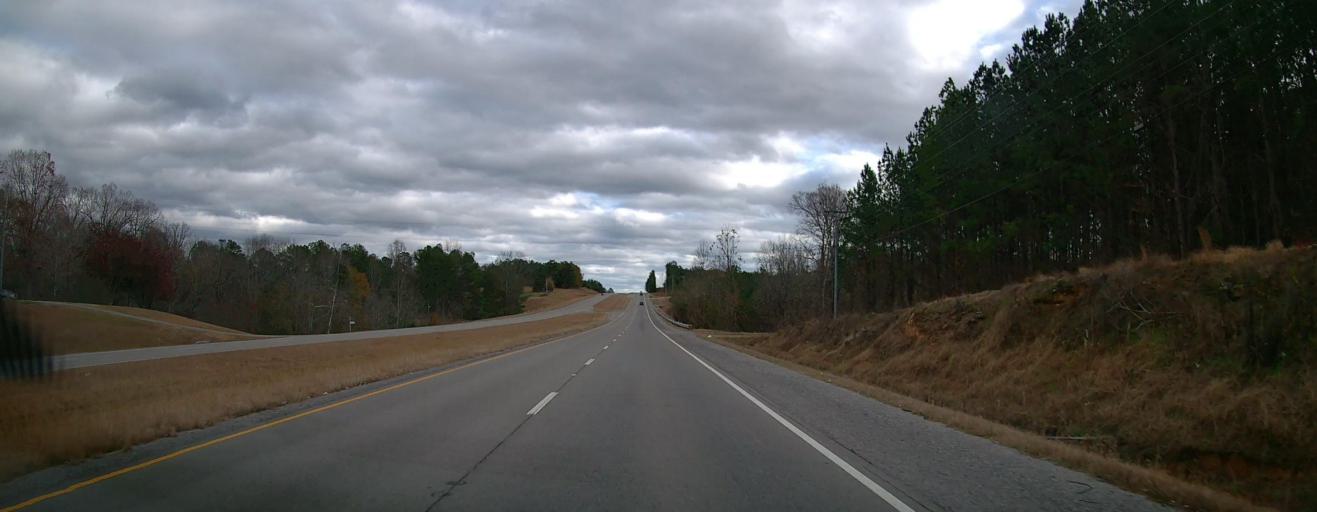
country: US
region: Alabama
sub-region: Lawrence County
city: Town Creek
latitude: 34.5826
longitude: -87.4136
